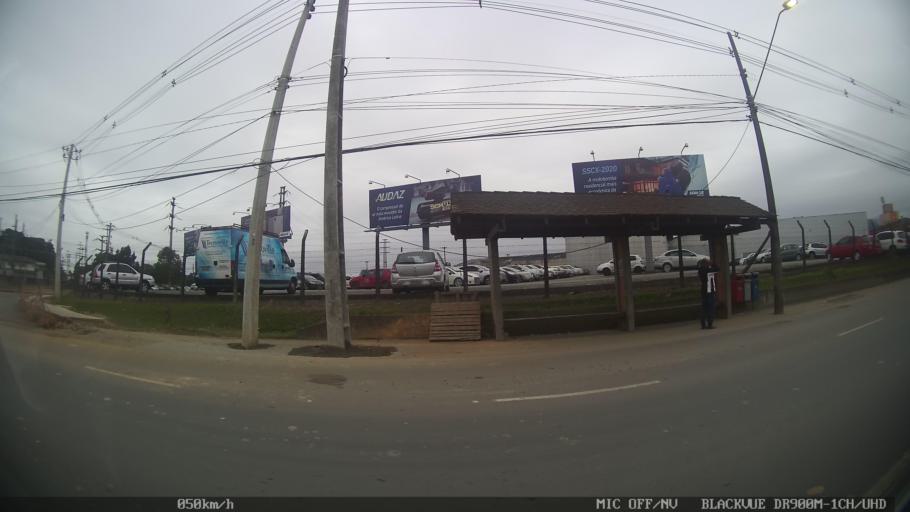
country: BR
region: Santa Catarina
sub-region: Joinville
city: Joinville
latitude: -26.2535
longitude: -48.8725
